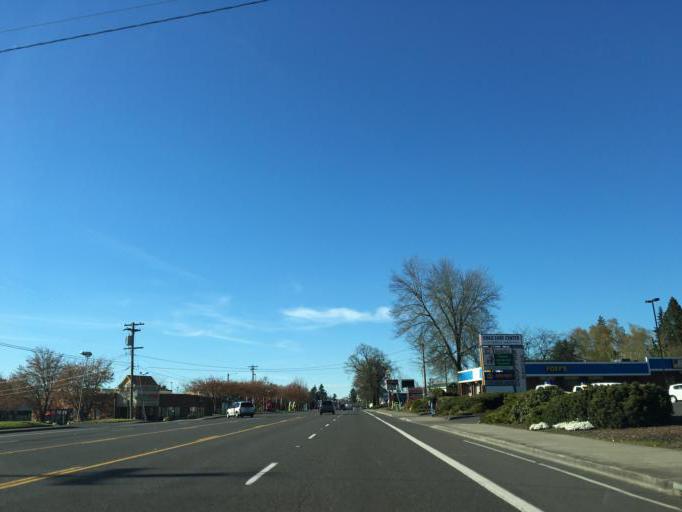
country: US
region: Oregon
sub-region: Clackamas County
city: Oak Grove
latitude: 45.4123
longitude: -122.6291
